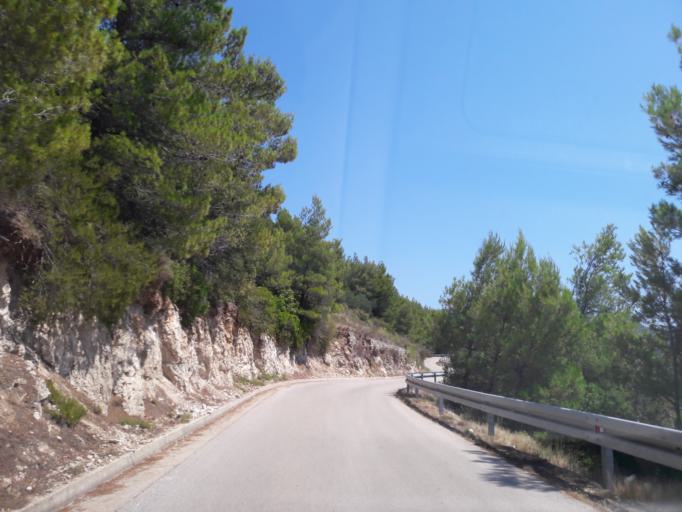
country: HR
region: Dubrovacko-Neretvanska
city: Blato
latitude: 42.9082
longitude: 17.4222
